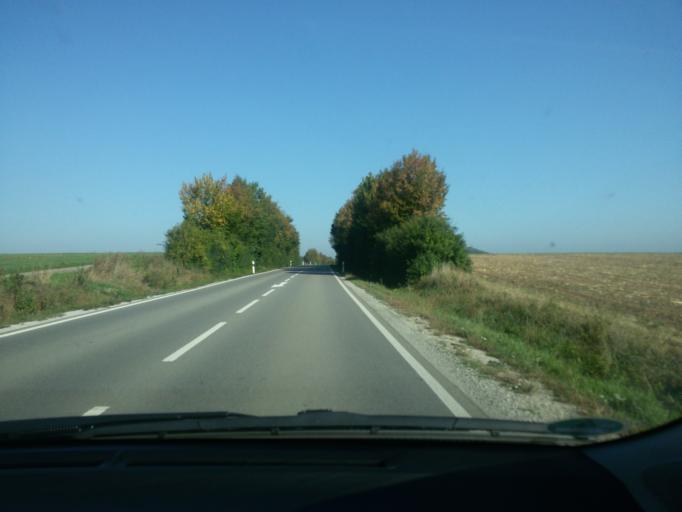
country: DE
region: Bavaria
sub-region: Swabia
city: Alerheim
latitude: 48.8369
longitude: 10.6310
